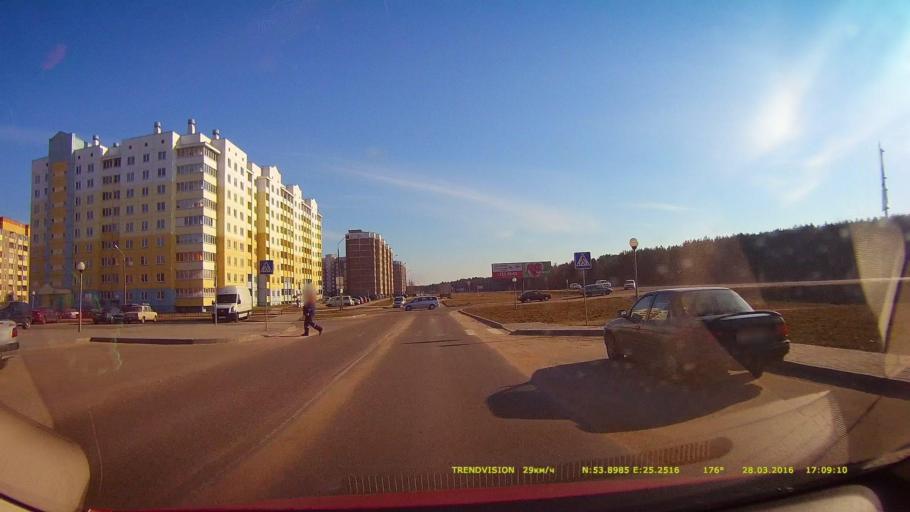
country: BY
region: Grodnenskaya
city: Lida
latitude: 53.8983
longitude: 25.2516
